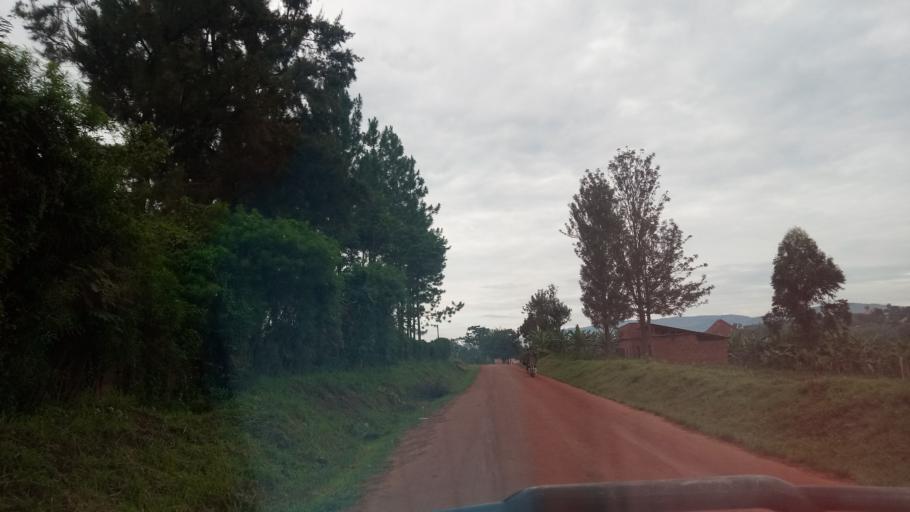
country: UG
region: Western Region
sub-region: Buhweju District
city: Buhweju
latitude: -0.1704
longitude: 30.4622
